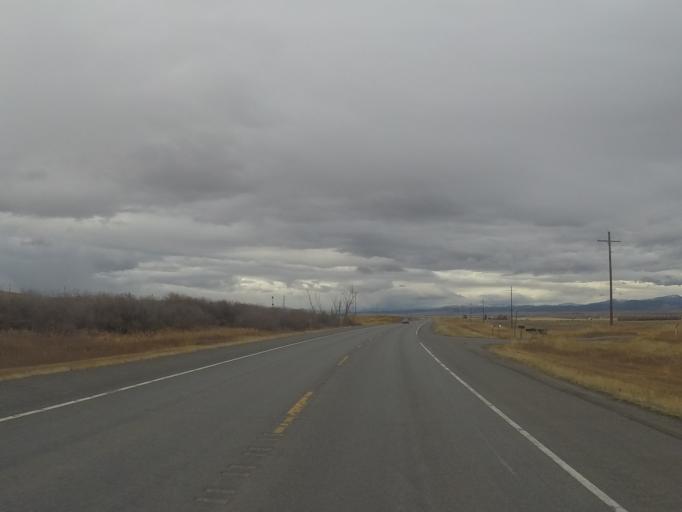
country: US
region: Montana
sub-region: Lewis and Clark County
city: East Helena
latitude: 46.5538
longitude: -111.7700
